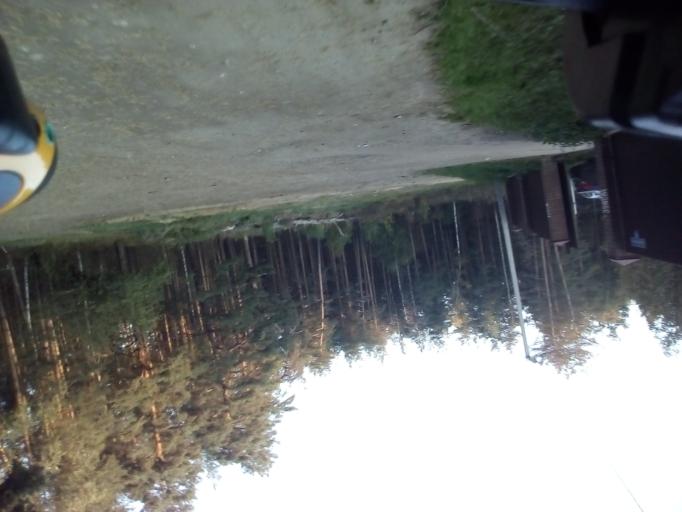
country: RU
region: Moskovskaya
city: Ramenskoye
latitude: 55.5879
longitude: 38.2298
